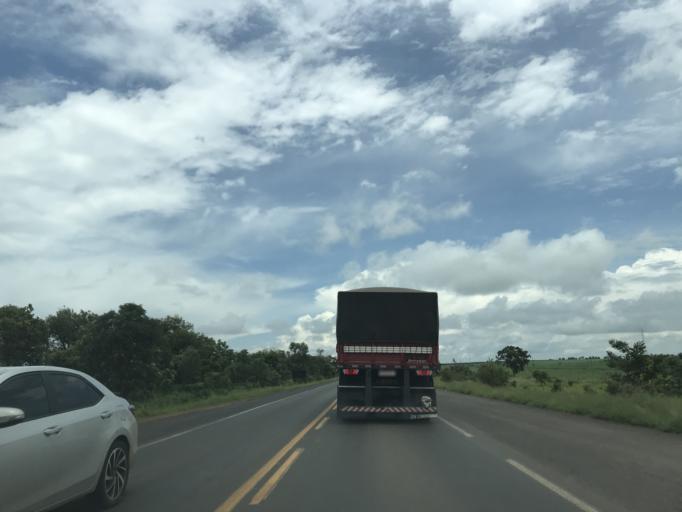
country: BR
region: Minas Gerais
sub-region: Frutal
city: Frutal
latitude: -19.7499
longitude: -48.9689
